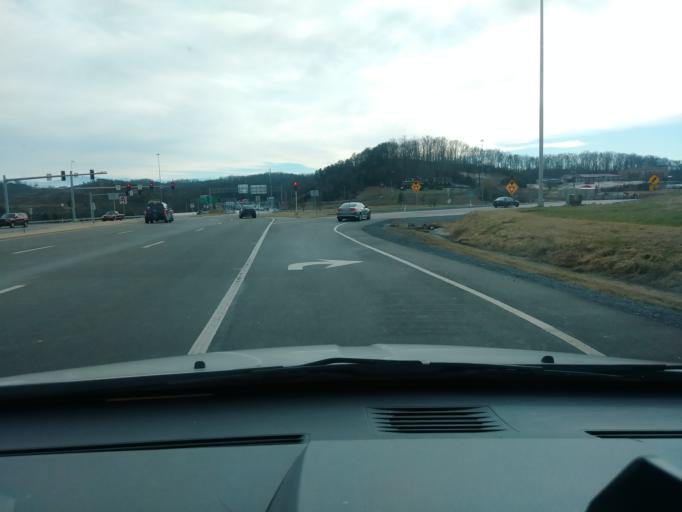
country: US
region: Tennessee
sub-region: Sevier County
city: Sevierville
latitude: 35.9859
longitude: -83.6087
